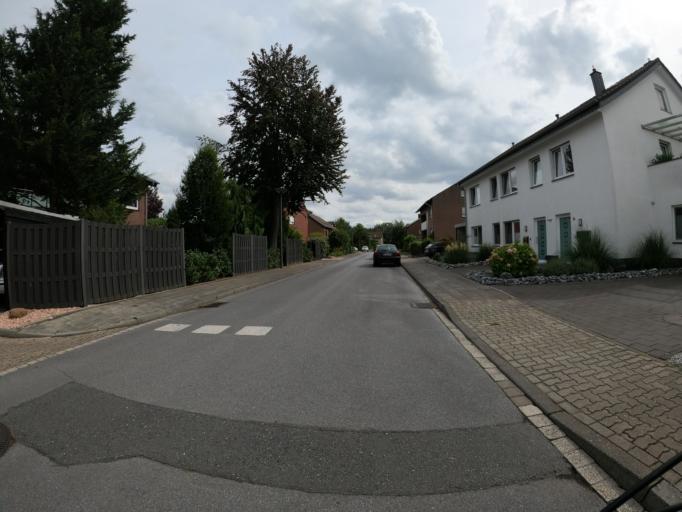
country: DE
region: North Rhine-Westphalia
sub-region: Regierungsbezirk Arnsberg
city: Lippstadt
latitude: 51.7052
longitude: 8.3308
